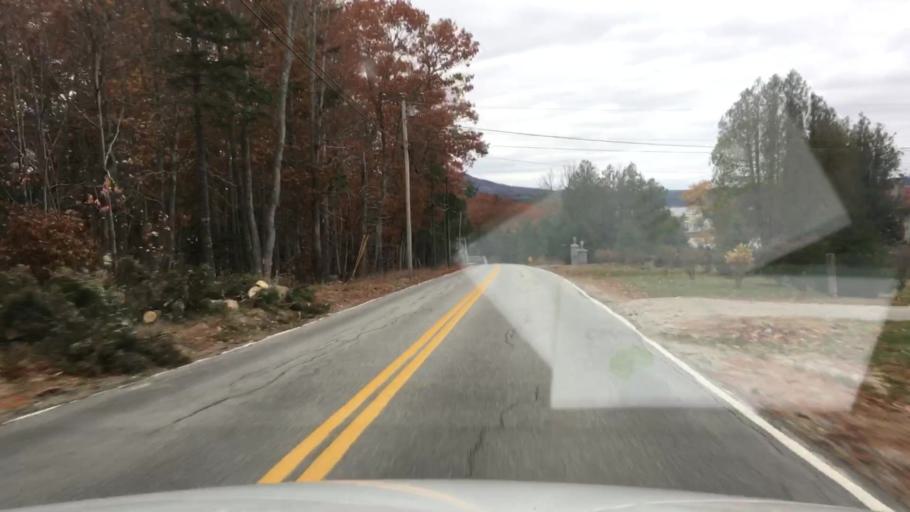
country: US
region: Maine
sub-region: Hancock County
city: Sedgwick
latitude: 44.3715
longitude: -68.5582
